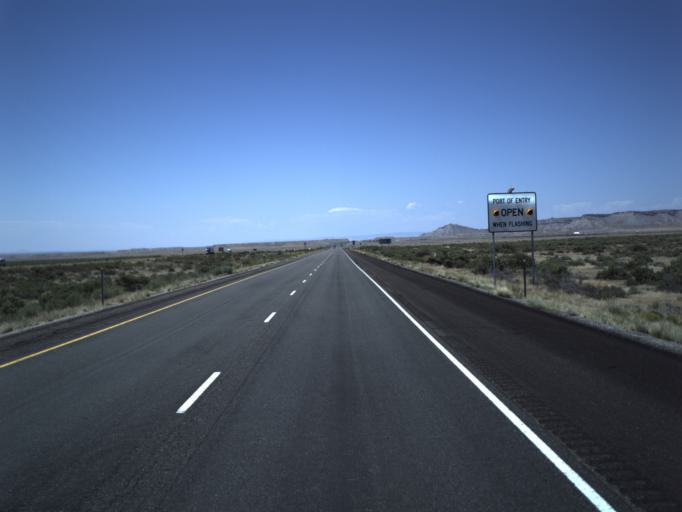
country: US
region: Utah
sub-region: Grand County
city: Moab
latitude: 38.9586
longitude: -109.7396
